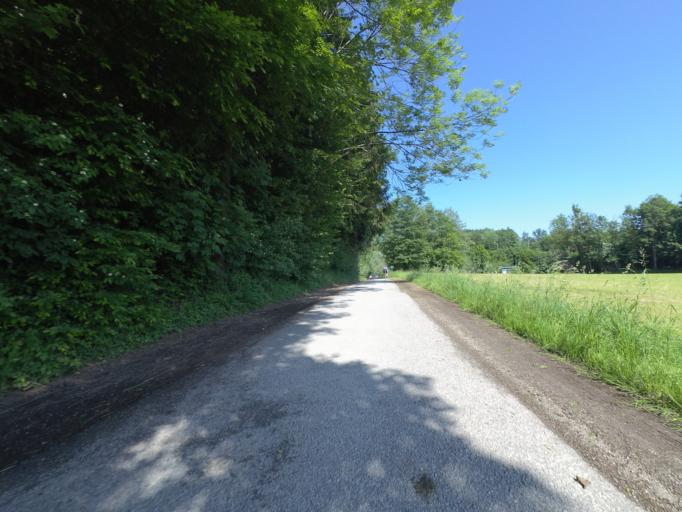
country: DE
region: Bavaria
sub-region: Upper Bavaria
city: Piding
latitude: 47.7676
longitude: 12.9556
